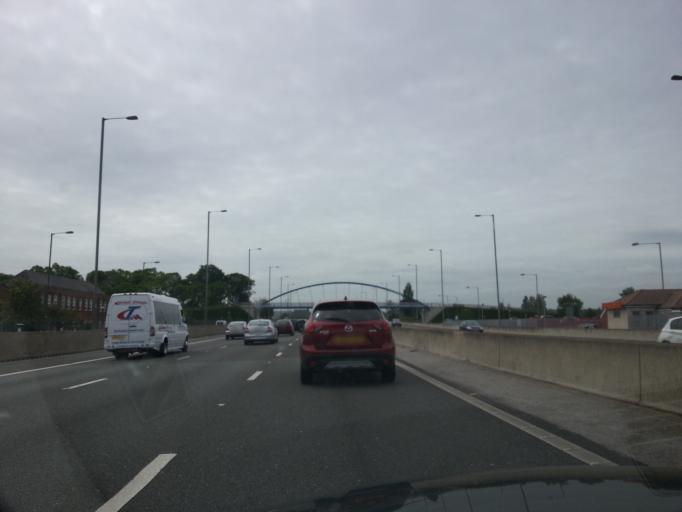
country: GB
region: England
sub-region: Cheshire West and Chester
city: Shotwick
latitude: 53.2243
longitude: -2.9976
